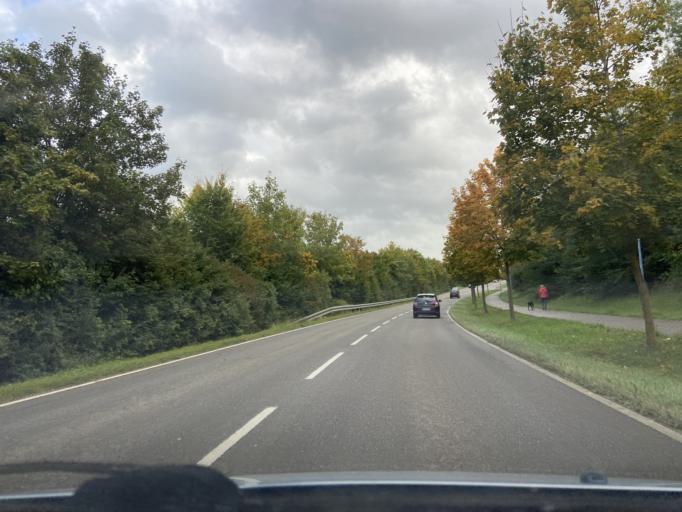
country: DE
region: Baden-Wuerttemberg
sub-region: Tuebingen Region
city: Sigmaringen
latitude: 48.0974
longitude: 9.2385
